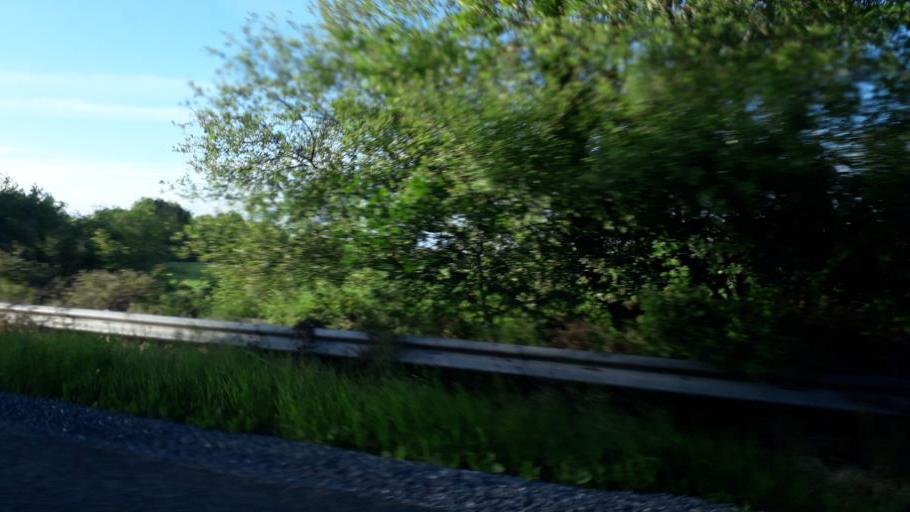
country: IE
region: Leinster
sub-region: Loch Garman
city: Loch Garman
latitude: 52.3611
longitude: -6.5098
